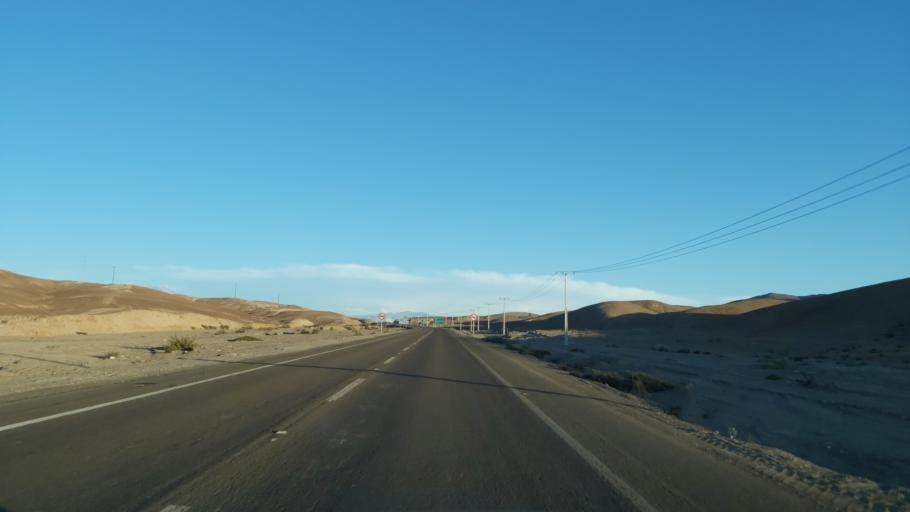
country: CL
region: Atacama
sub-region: Provincia de Chanaral
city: Diego de Almagro
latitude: -26.4138
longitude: -70.0332
